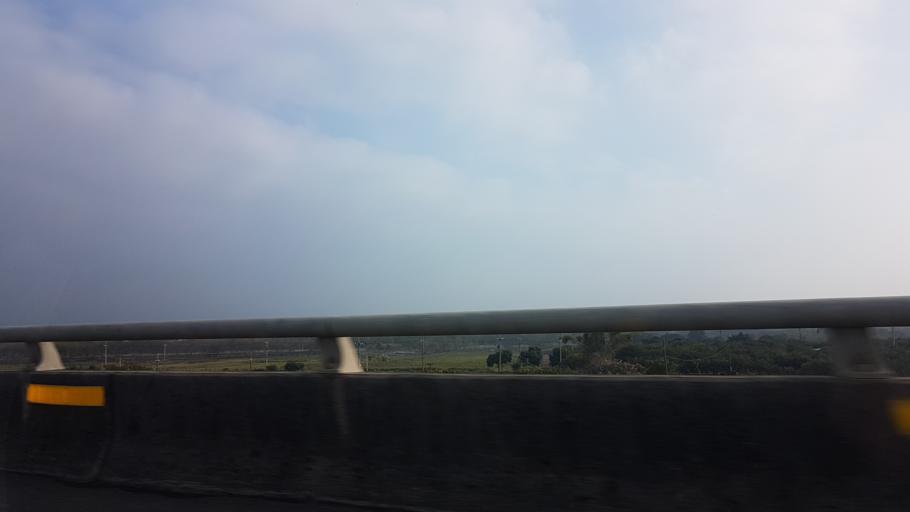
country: TW
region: Taiwan
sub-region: Chiayi
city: Jiayi Shi
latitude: 23.4168
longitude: 120.4000
